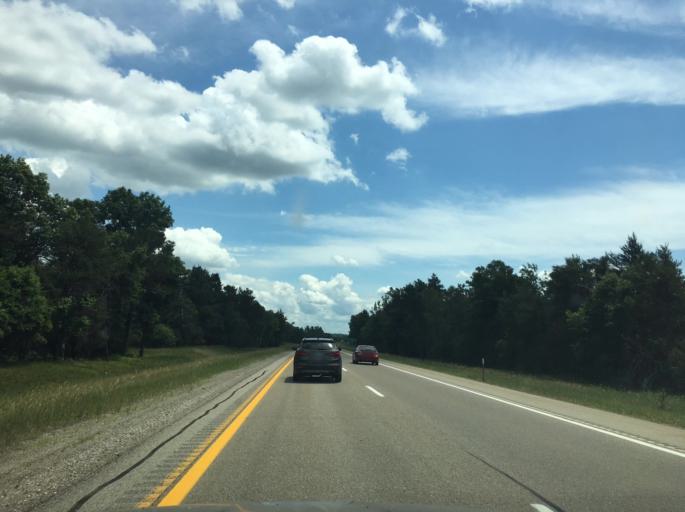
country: US
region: Michigan
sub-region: Roscommon County
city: Roscommon
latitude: 44.5274
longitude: -84.6751
